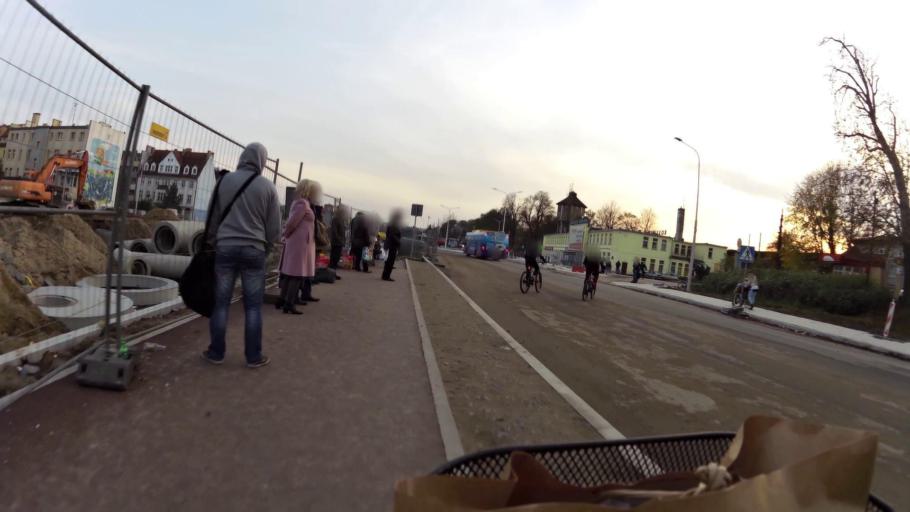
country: PL
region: West Pomeranian Voivodeship
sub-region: Koszalin
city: Koszalin
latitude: 54.1917
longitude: 16.1712
